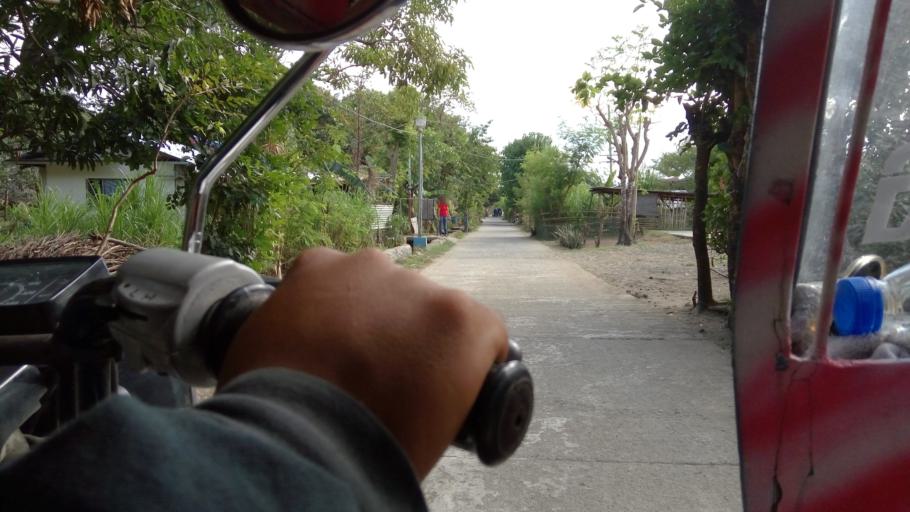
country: PH
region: Ilocos
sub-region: Province of La Union
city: San Eugenio
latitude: 16.3584
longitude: 120.3526
